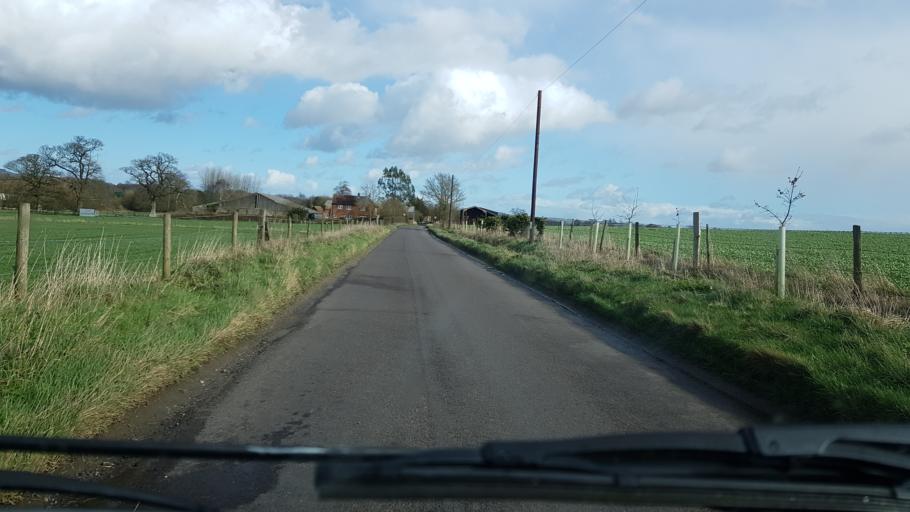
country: GB
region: England
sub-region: Wiltshire
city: Woodborough
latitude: 51.3337
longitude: -1.8550
